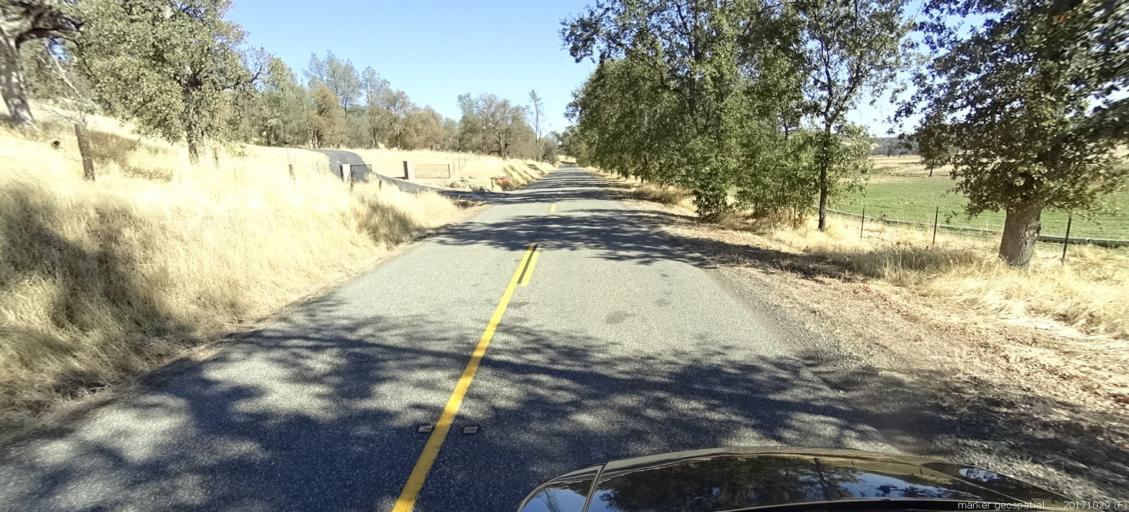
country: US
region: California
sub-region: Shasta County
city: Shasta
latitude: 40.4756
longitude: -122.6107
